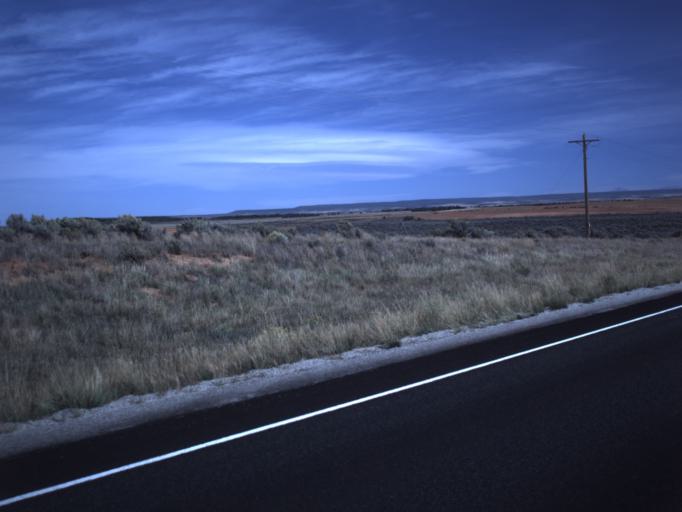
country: US
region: Utah
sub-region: San Juan County
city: Monticello
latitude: 37.8459
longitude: -109.1462
